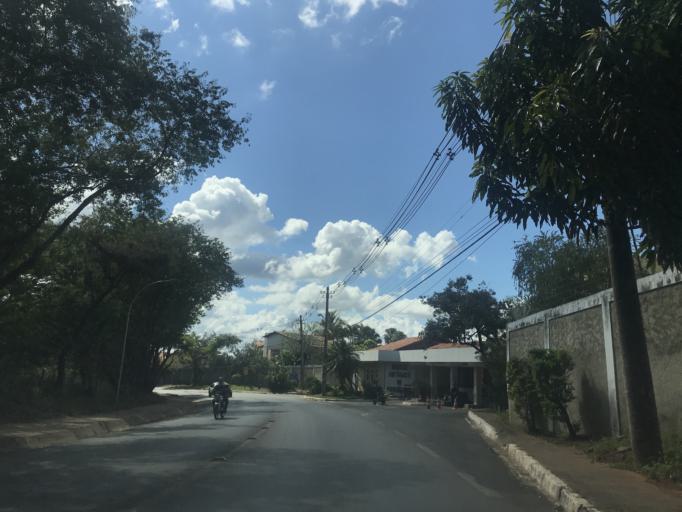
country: BR
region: Federal District
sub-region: Brasilia
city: Brasilia
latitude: -15.8820
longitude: -47.8071
